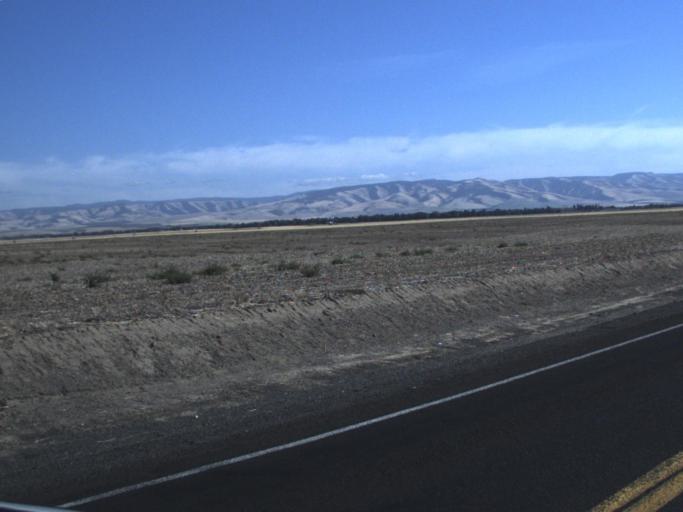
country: US
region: Washington
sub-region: Walla Walla County
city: Walla Walla
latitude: 46.0995
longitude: -118.3709
